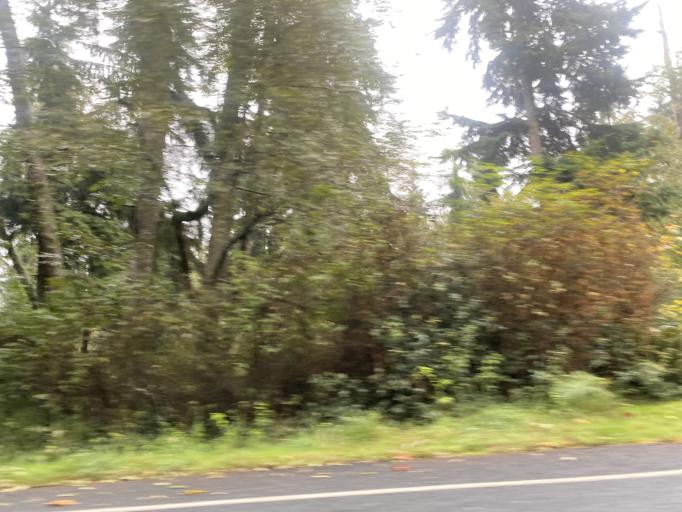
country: US
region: Washington
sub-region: Island County
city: Langley
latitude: 48.0429
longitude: -122.4305
